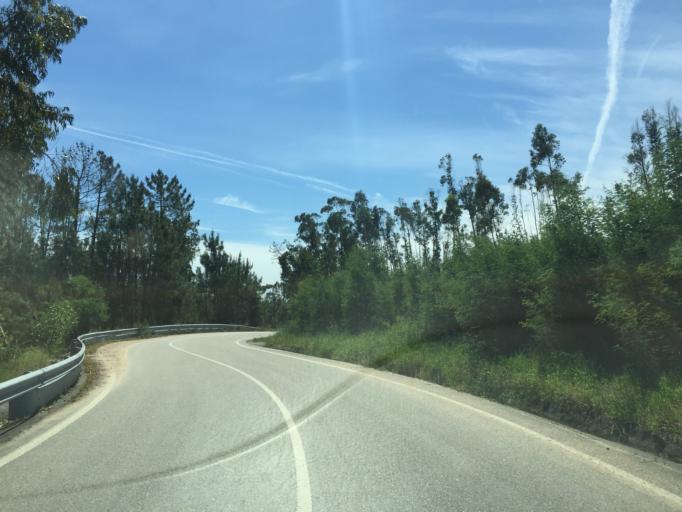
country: PT
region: Coimbra
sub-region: Figueira da Foz
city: Lavos
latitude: 40.0776
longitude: -8.7779
